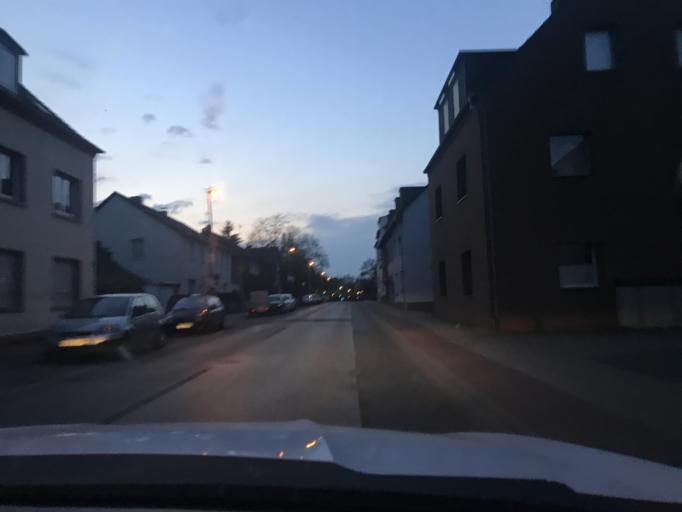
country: DE
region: North Rhine-Westphalia
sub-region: Regierungsbezirk Dusseldorf
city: Hochfeld
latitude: 51.3894
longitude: 6.7056
